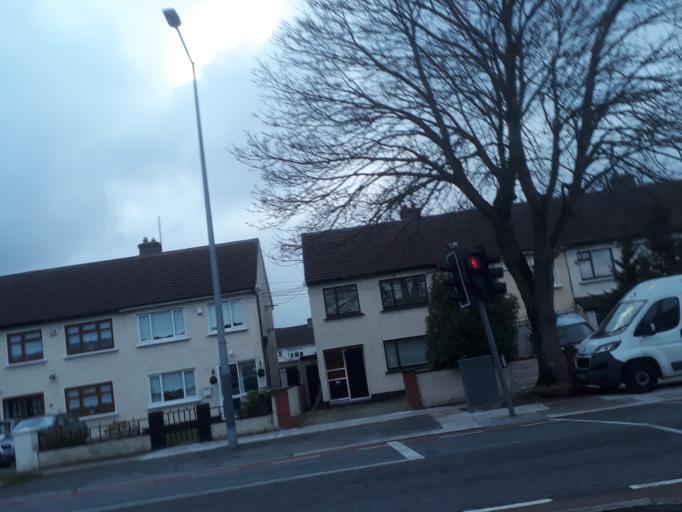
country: IE
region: Leinster
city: Crumlin
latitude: 53.3120
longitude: -6.3274
